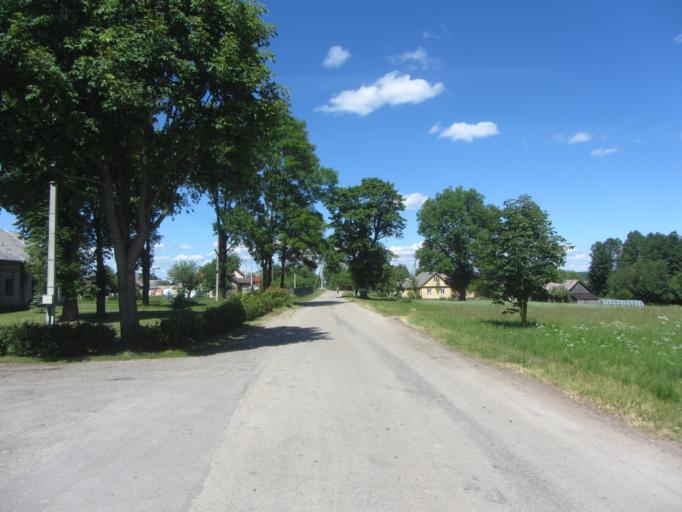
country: LT
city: Jieznas
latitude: 54.7036
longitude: 24.2212
